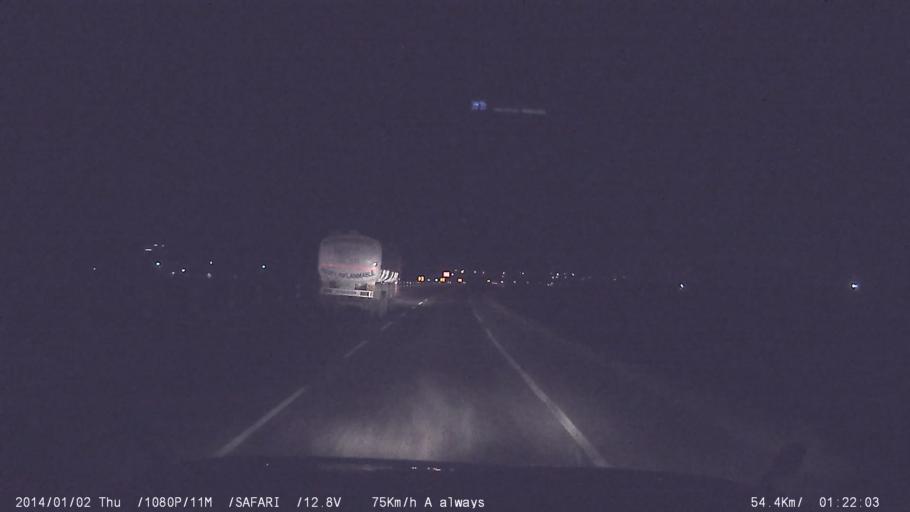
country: IN
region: Tamil Nadu
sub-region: Coimbatore
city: Irugur
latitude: 11.0493
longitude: 77.0787
